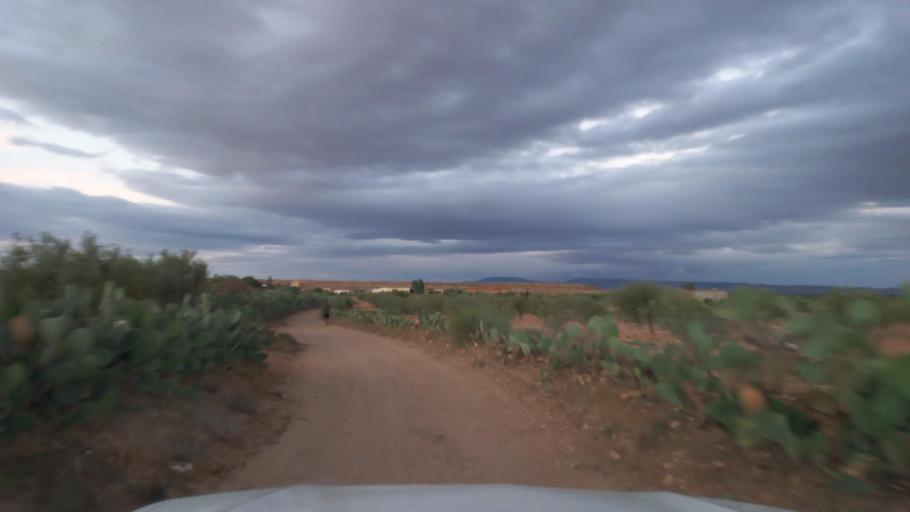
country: TN
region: Al Qasrayn
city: Kasserine
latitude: 35.2564
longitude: 8.9404
